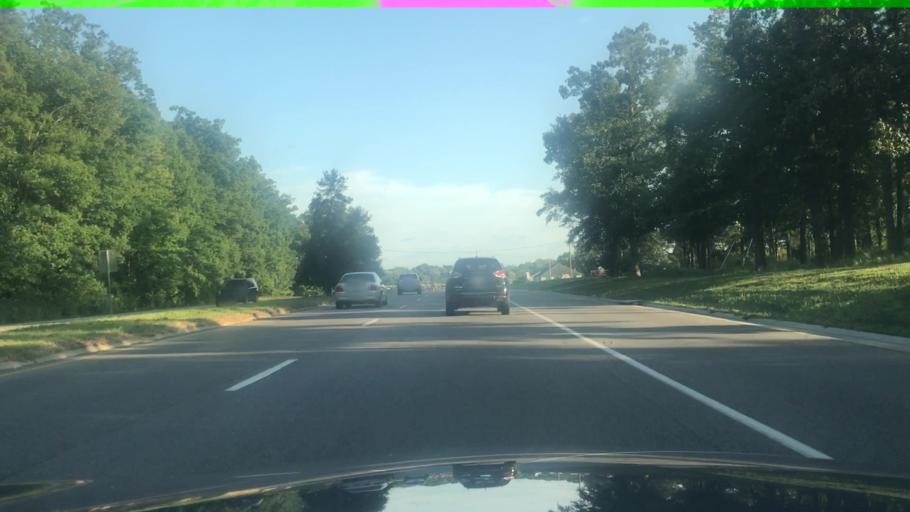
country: US
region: Virginia
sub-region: Chesterfield County
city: Brandermill
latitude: 37.4472
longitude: -77.5835
